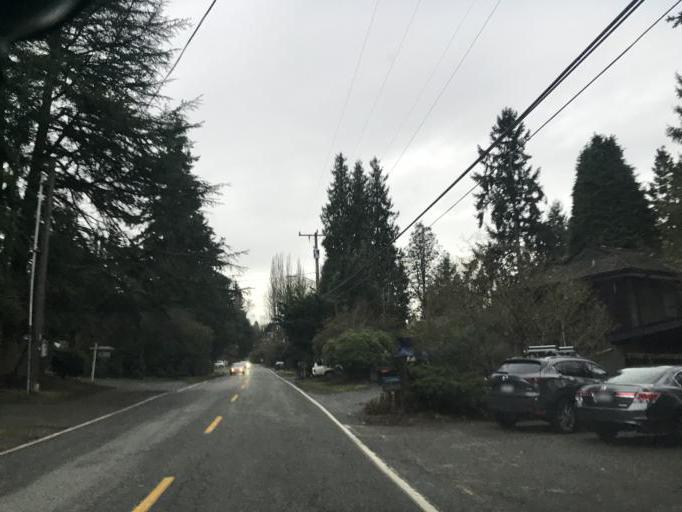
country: US
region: Washington
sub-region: King County
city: Lake Forest Park
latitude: 47.7040
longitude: -122.2983
